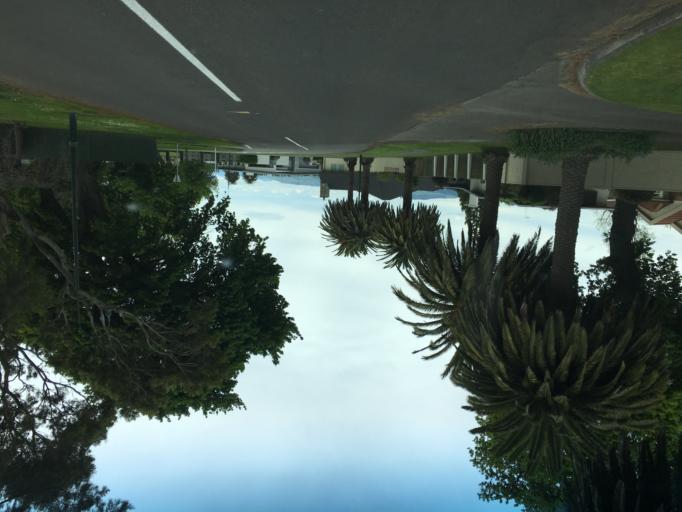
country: NZ
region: Manawatu-Wanganui
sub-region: Palmerston North City
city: Palmerston North
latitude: -40.3785
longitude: 175.5783
